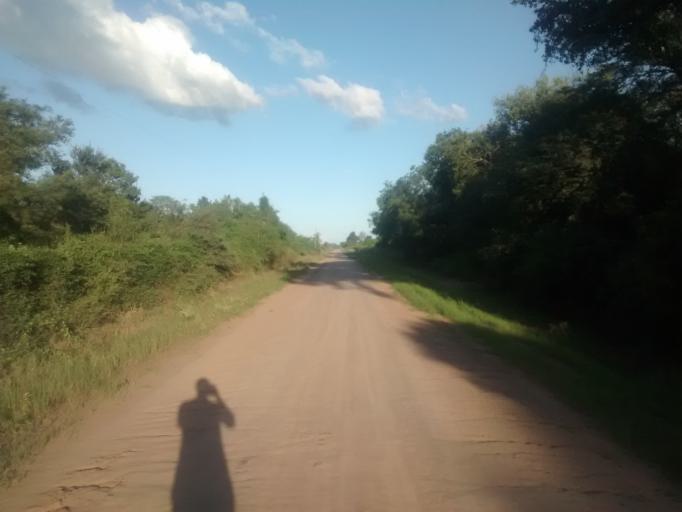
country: AR
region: Chaco
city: Presidencia Roque Saenz Pena
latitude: -26.7419
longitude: -60.3132
